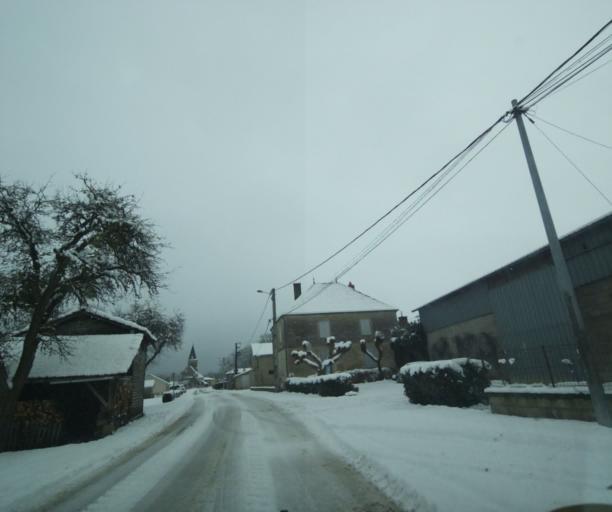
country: FR
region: Champagne-Ardenne
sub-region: Departement de la Haute-Marne
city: Montier-en-Der
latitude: 48.5363
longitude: 4.8119
